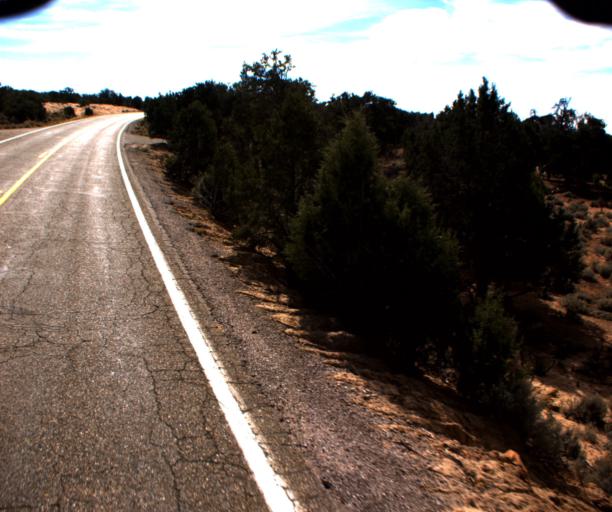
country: US
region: Arizona
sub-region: Navajo County
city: Kayenta
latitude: 36.6030
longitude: -110.4981
